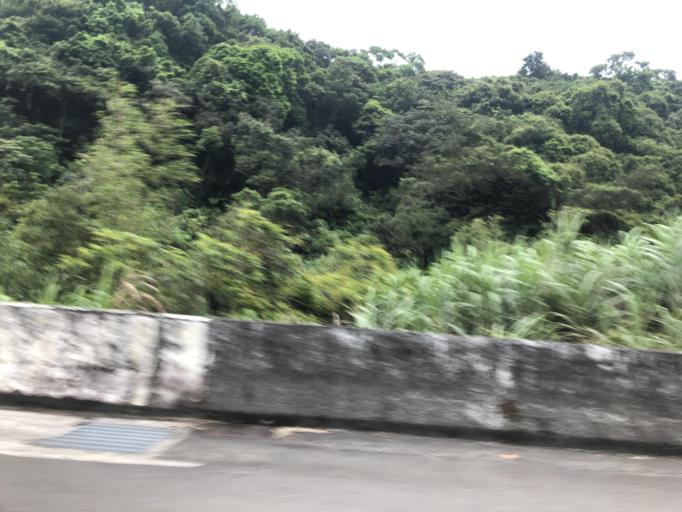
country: TW
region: Taiwan
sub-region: Keelung
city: Keelung
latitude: 25.2009
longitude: 121.6841
